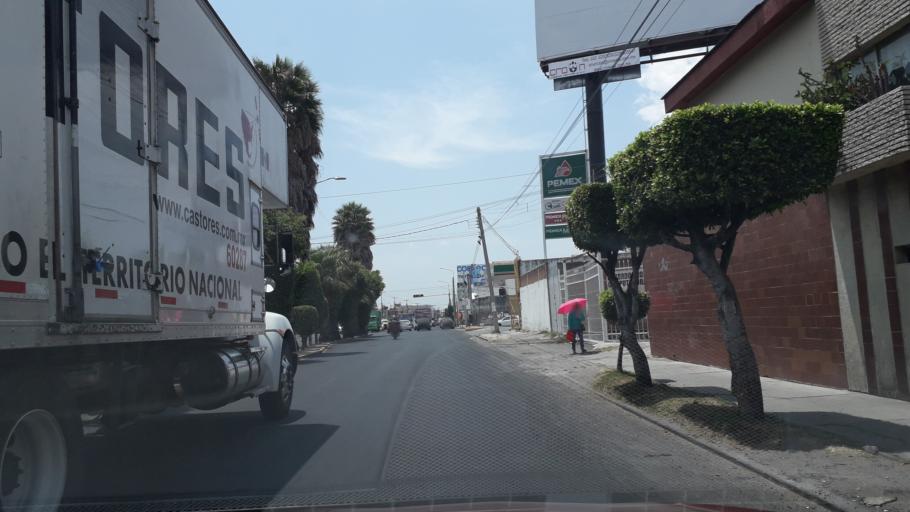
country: MX
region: Puebla
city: Puebla
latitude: 19.0185
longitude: -98.1924
